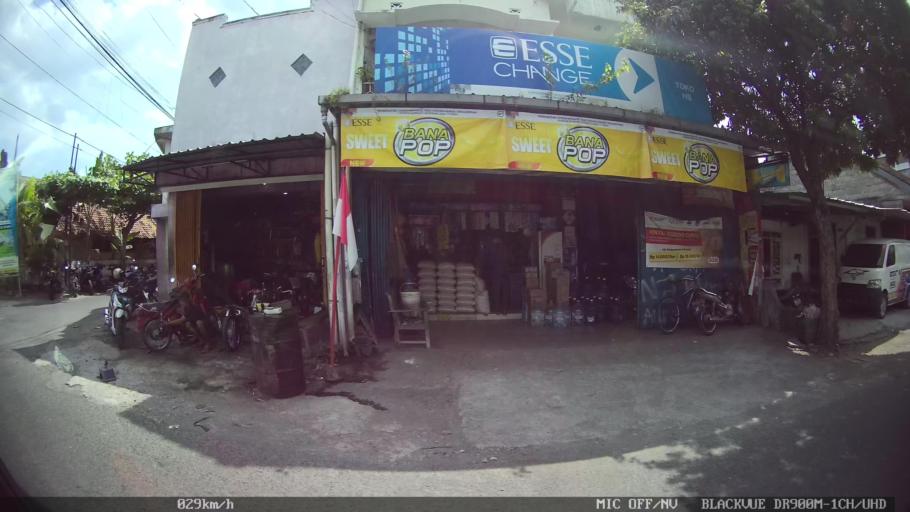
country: ID
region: Daerah Istimewa Yogyakarta
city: Gamping Lor
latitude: -7.8102
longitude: 110.3384
